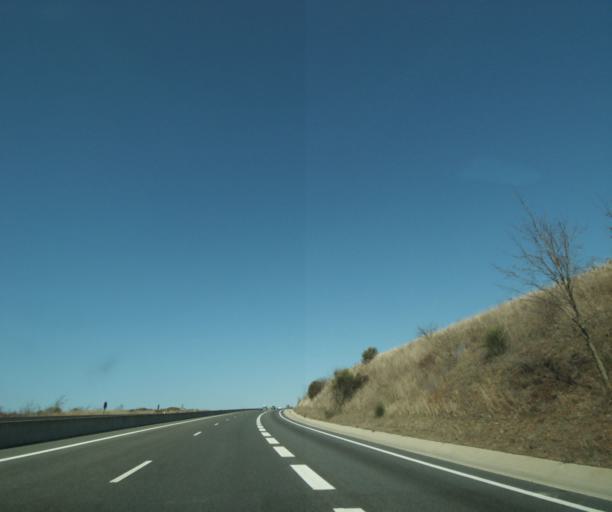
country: FR
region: Midi-Pyrenees
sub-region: Departement de l'Aveyron
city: Severac-le-Chateau
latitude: 44.2341
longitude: 3.0622
